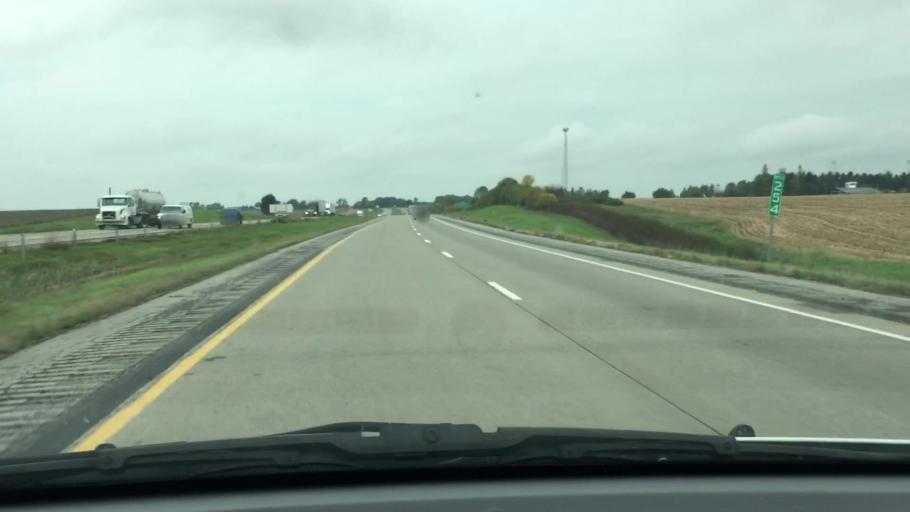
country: US
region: Iowa
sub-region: Cedar County
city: West Branch
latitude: 41.6646
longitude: -91.3587
